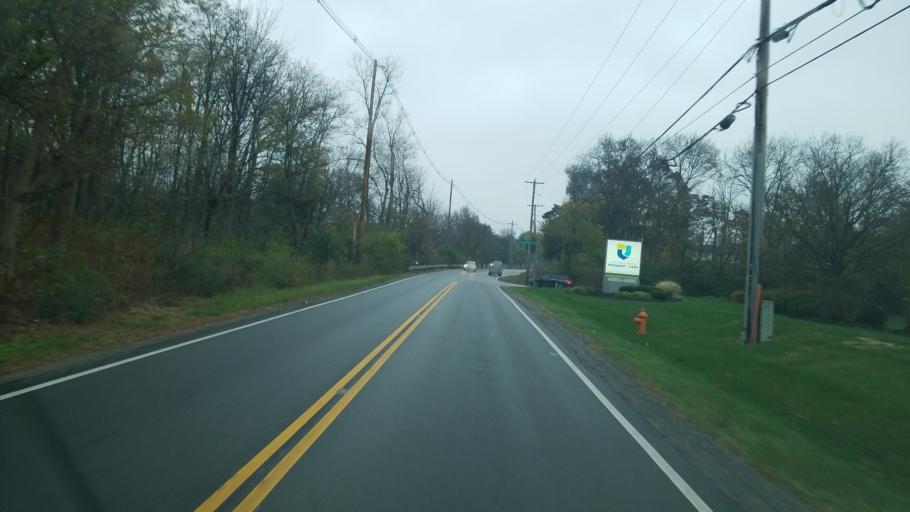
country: US
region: Ohio
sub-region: Franklin County
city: Worthington
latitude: 40.0603
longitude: -83.0357
